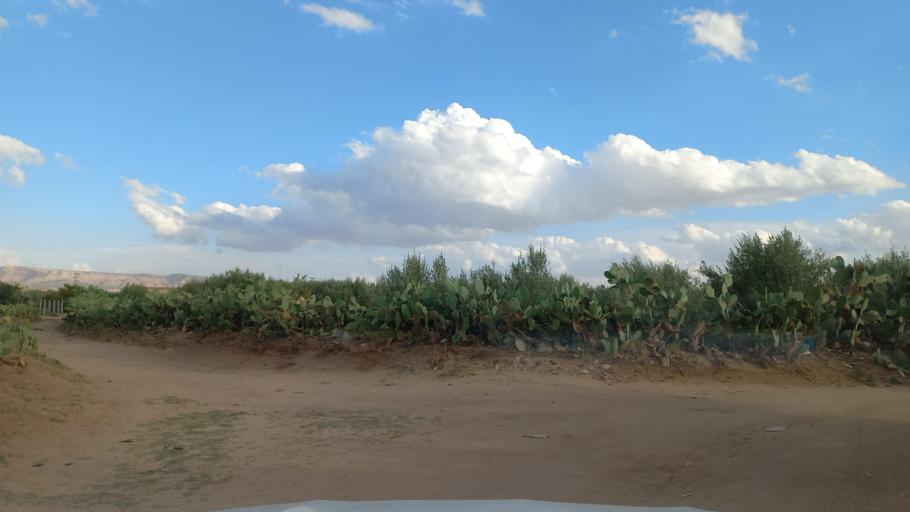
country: TN
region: Al Qasrayn
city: Sbiba
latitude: 35.3833
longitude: 9.0548
